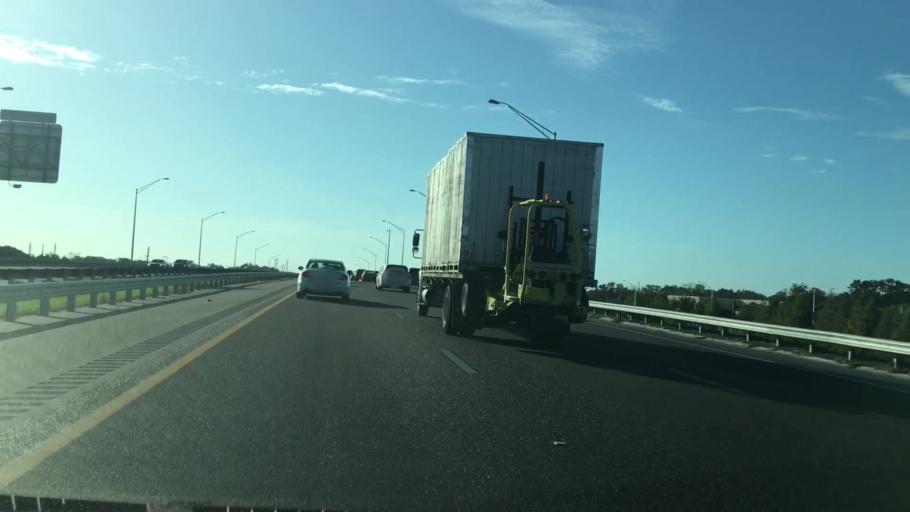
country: US
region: Florida
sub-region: Orange County
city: Azalea Park
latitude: 28.5119
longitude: -81.2489
